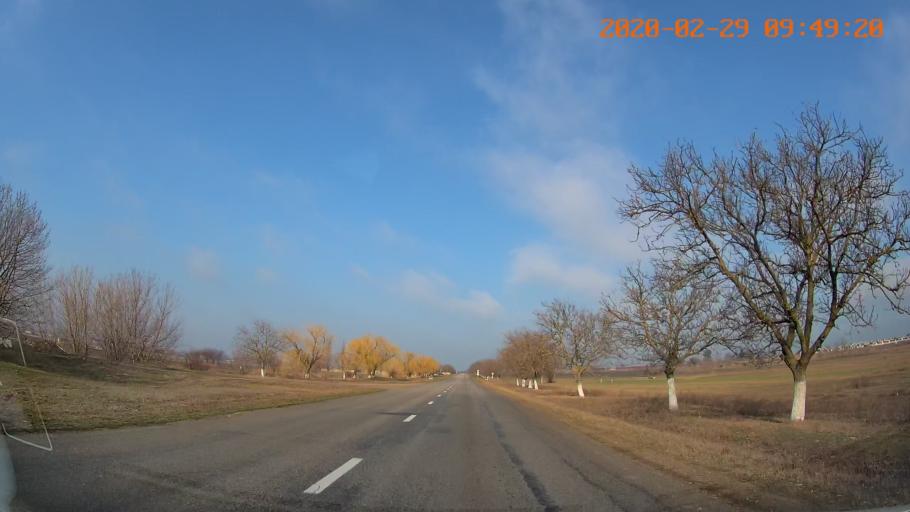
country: MD
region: Telenesti
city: Crasnoe
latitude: 46.6964
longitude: 29.7736
